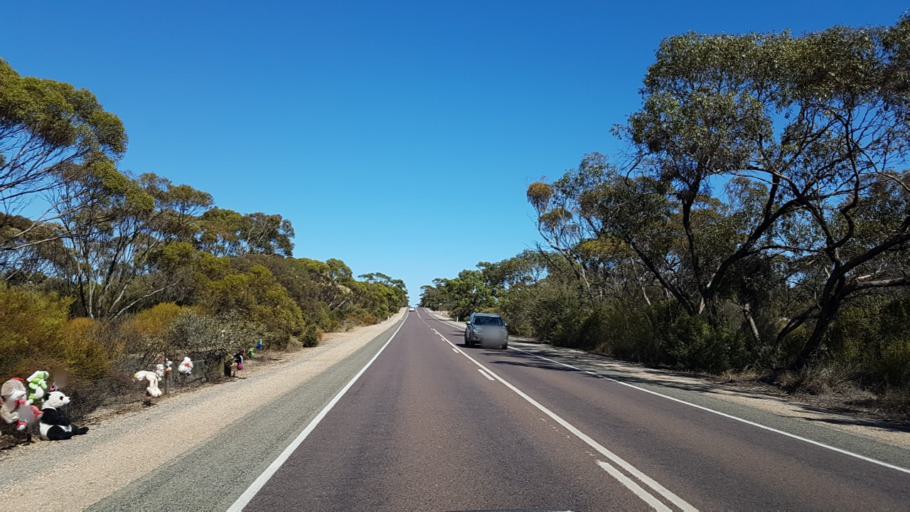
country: AU
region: South Australia
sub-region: Copper Coast
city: Kadina
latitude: -34.0486
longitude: 137.9678
